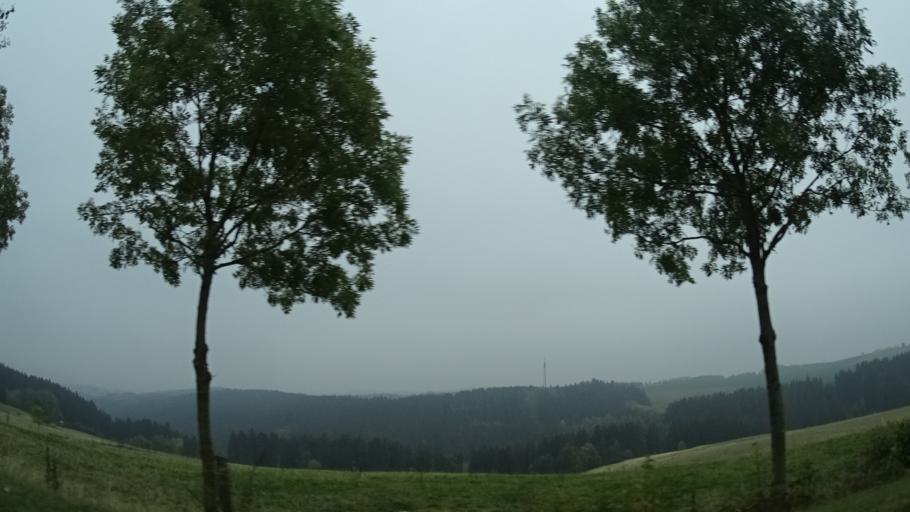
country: DE
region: Thuringia
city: Herschdorf
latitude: 50.6367
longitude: 11.0523
